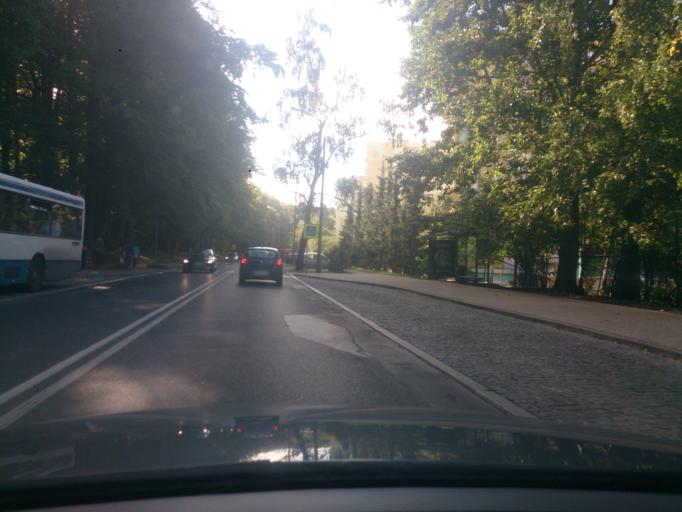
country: PL
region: Pomeranian Voivodeship
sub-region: Sopot
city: Sopot
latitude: 54.4560
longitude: 18.5318
